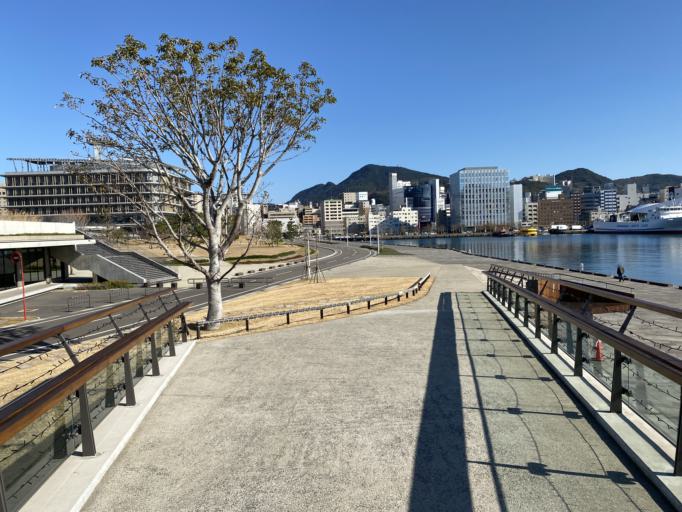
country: JP
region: Nagasaki
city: Nagasaki-shi
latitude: 32.7491
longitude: 129.8671
